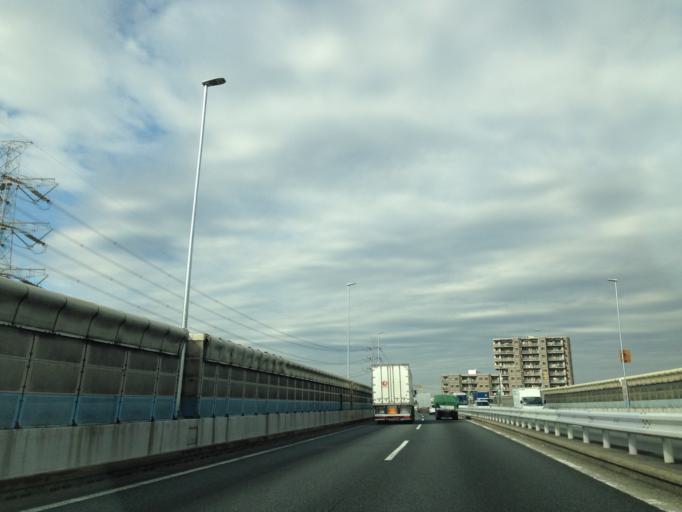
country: JP
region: Saitama
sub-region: Kawaguchi-shi
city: Hatogaya-honcho
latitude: 35.8432
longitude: 139.7500
